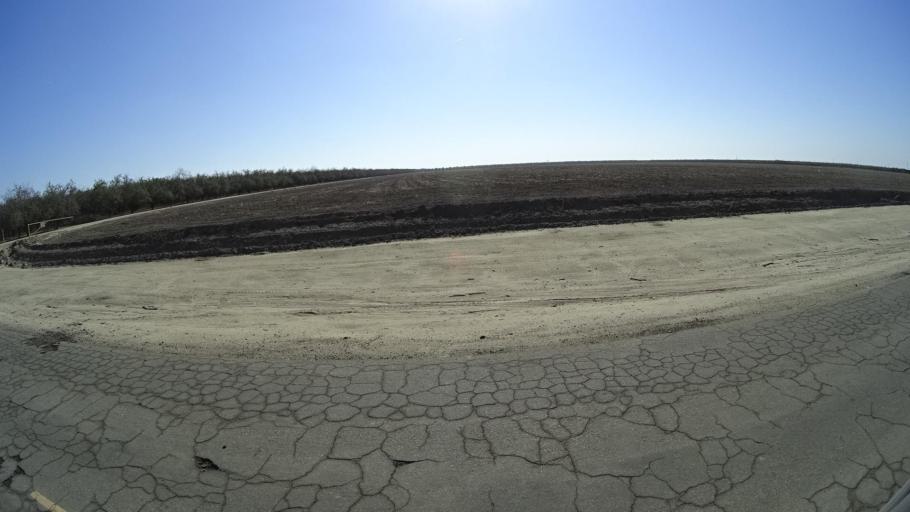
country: US
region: California
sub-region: Kern County
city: McFarland
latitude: 35.7035
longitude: -119.1652
